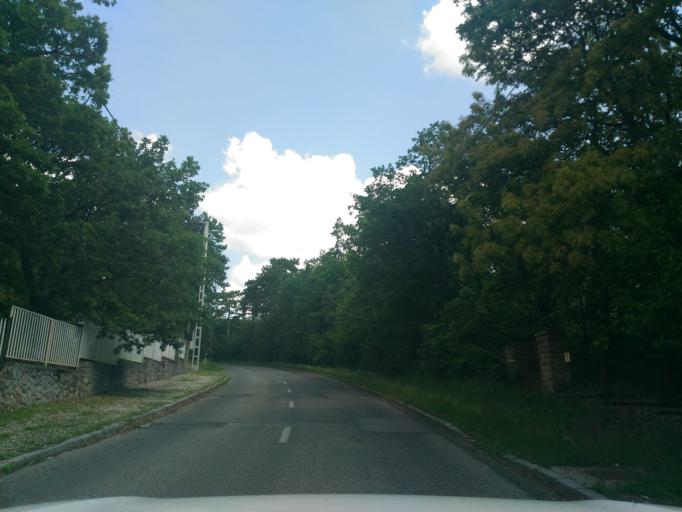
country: HU
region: Baranya
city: Pecs
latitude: 46.0904
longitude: 18.2294
